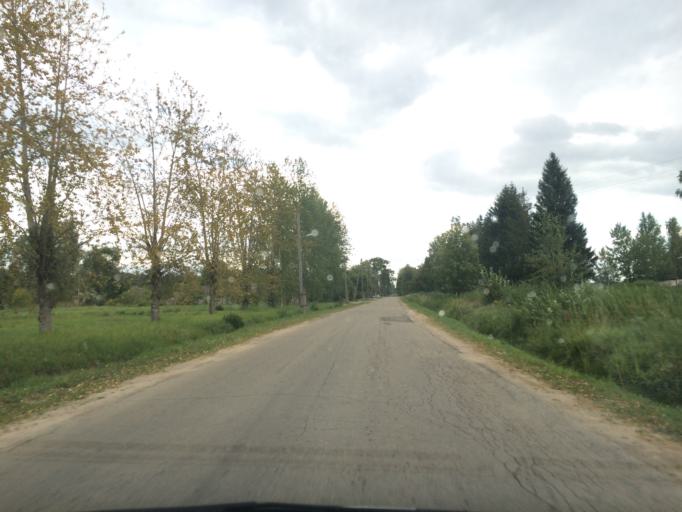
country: LV
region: Plavinu
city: Plavinas
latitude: 56.6198
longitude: 25.7483
